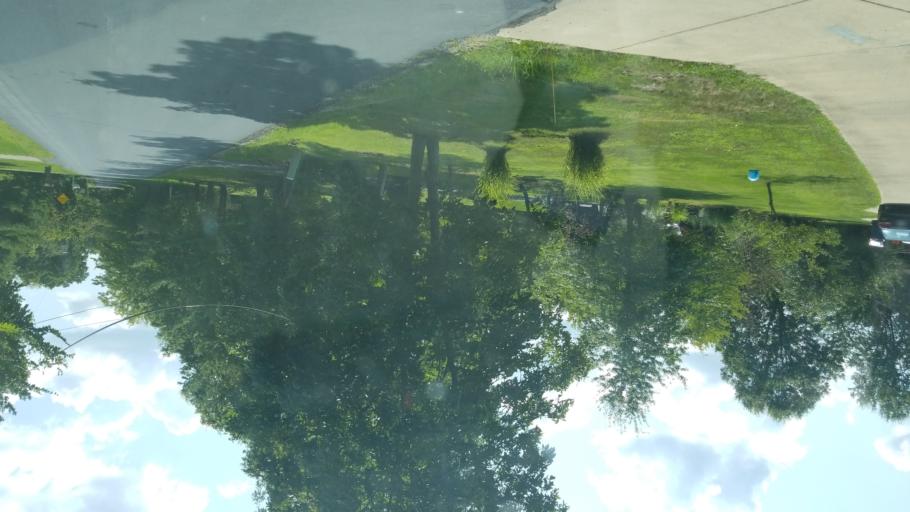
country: US
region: Ohio
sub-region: Delaware County
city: Lewis Center
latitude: 40.2530
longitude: -82.9464
